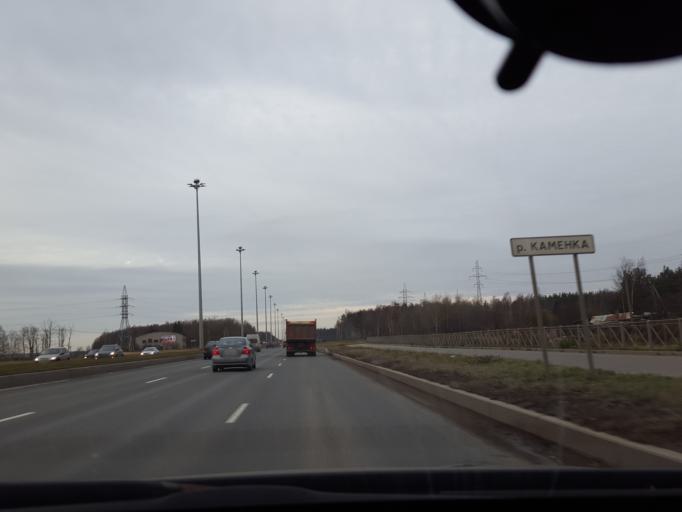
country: RU
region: Leningrad
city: Untolovo
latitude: 60.0430
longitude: 30.2386
